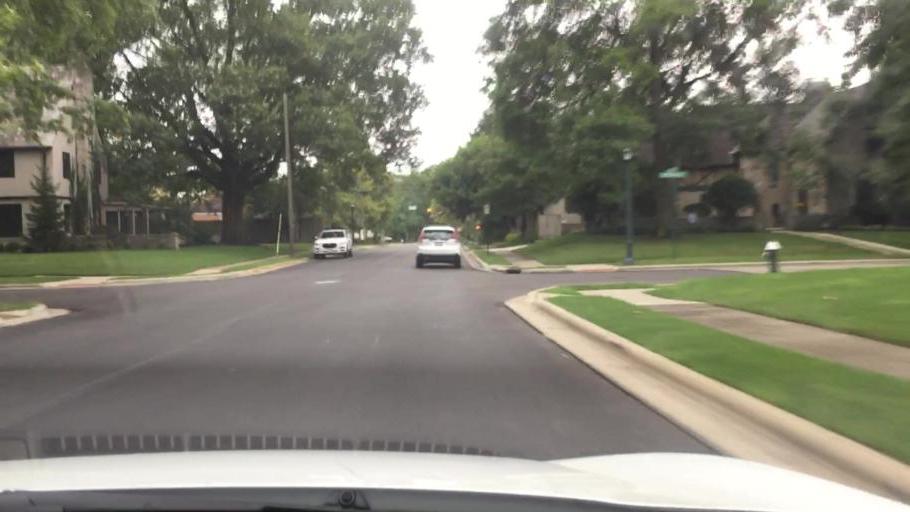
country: US
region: Ohio
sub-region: Franklin County
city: Bexley
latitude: 39.9582
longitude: -82.9274
